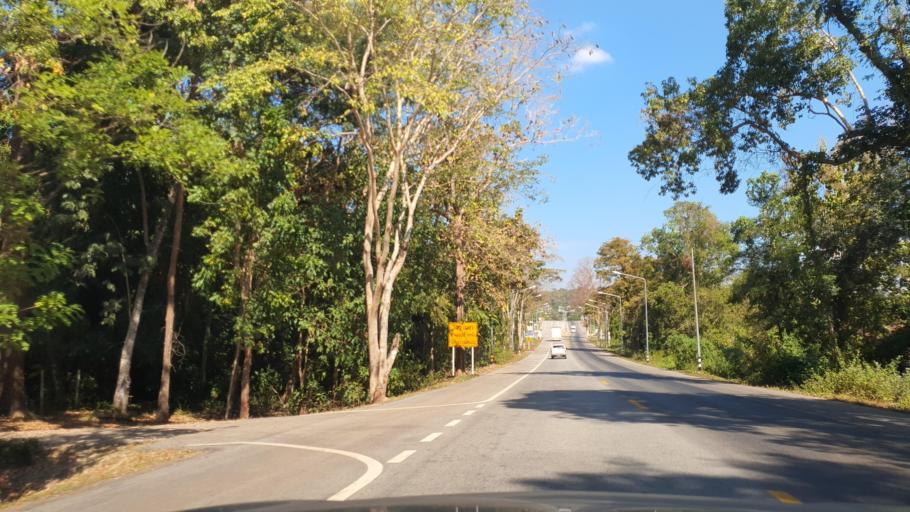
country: TH
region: Kalasin
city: Na Khu
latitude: 16.8541
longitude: 103.9302
